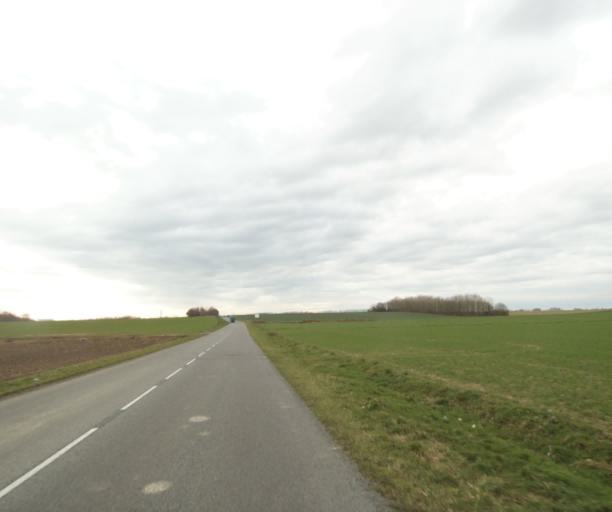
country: FR
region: Nord-Pas-de-Calais
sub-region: Departement du Nord
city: Sebourg
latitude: 50.3331
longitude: 3.6356
